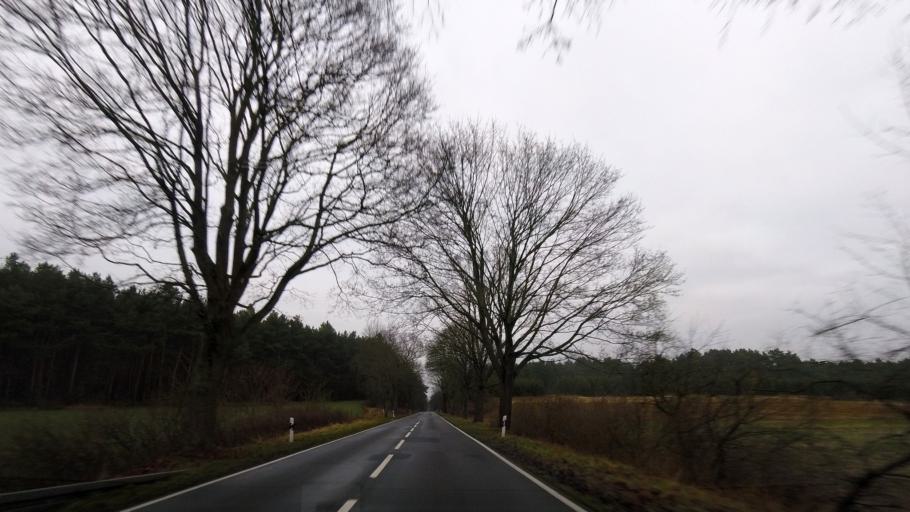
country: DE
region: Brandenburg
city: Treuenbrietzen
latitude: 52.0606
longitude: 12.9410
